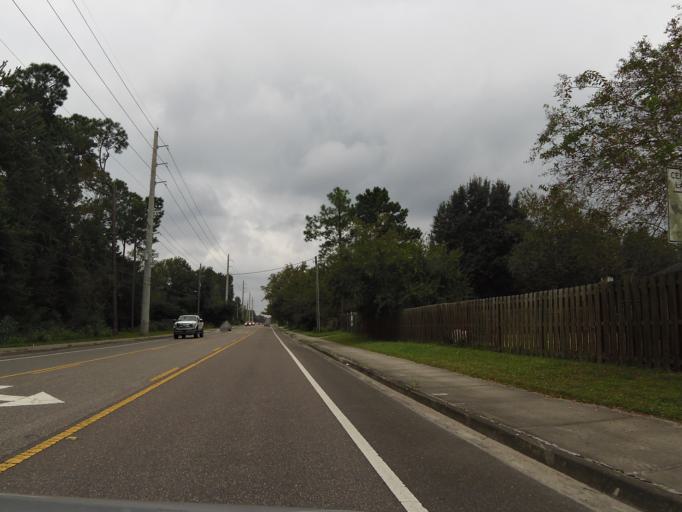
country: US
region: Florida
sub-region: Clay County
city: Bellair-Meadowbrook Terrace
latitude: 30.2083
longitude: -81.7648
